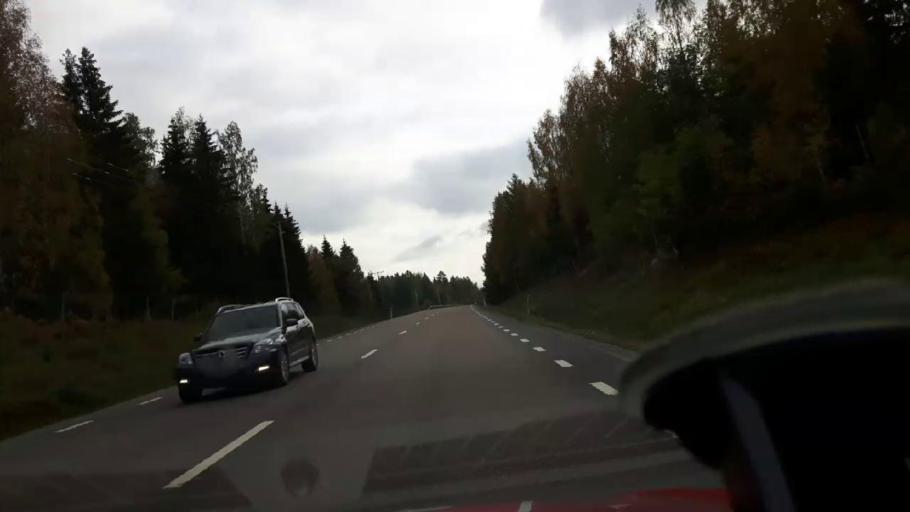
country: SE
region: Gaevleborg
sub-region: Bollnas Kommun
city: Kilafors
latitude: 61.2895
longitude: 16.5067
